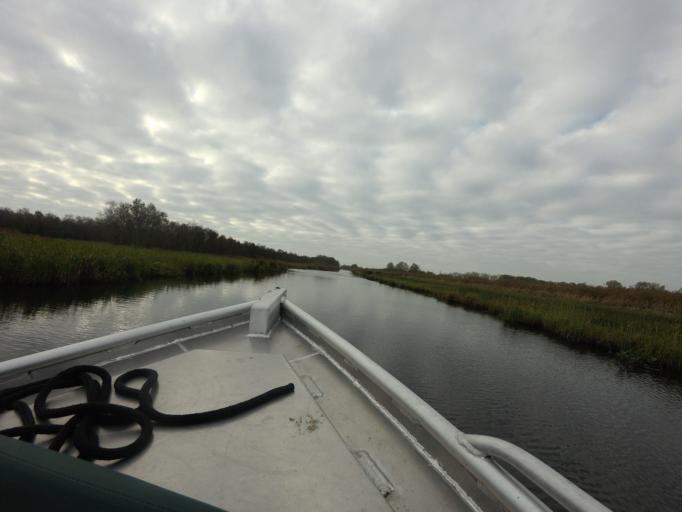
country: NL
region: Overijssel
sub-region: Gemeente Steenwijkerland
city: Oldemarkt
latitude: 52.8036
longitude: 5.9163
